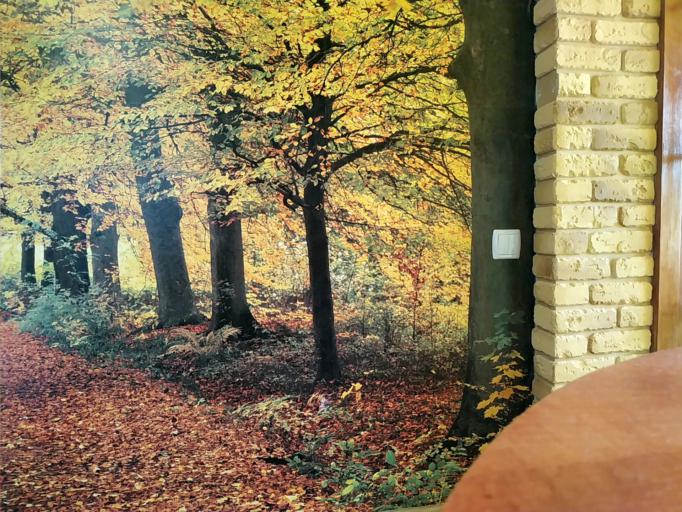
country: RU
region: Pskov
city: Dno
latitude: 57.9117
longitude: 30.1733
